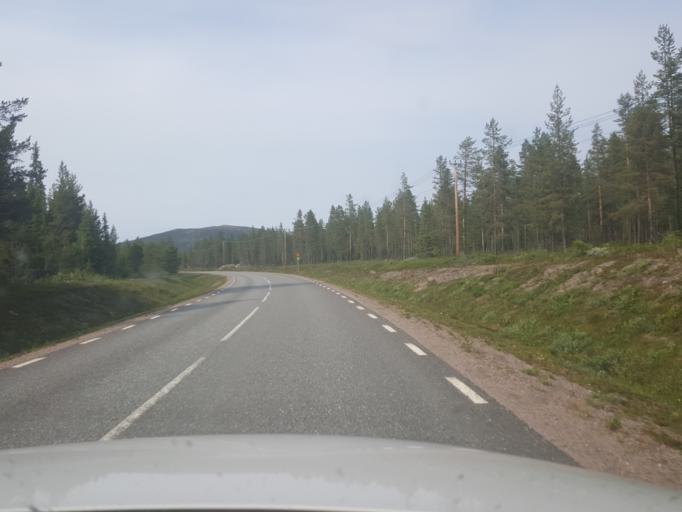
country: SE
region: Norrbotten
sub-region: Arjeplogs Kommun
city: Arjeplog
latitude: 65.8478
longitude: 18.0428
